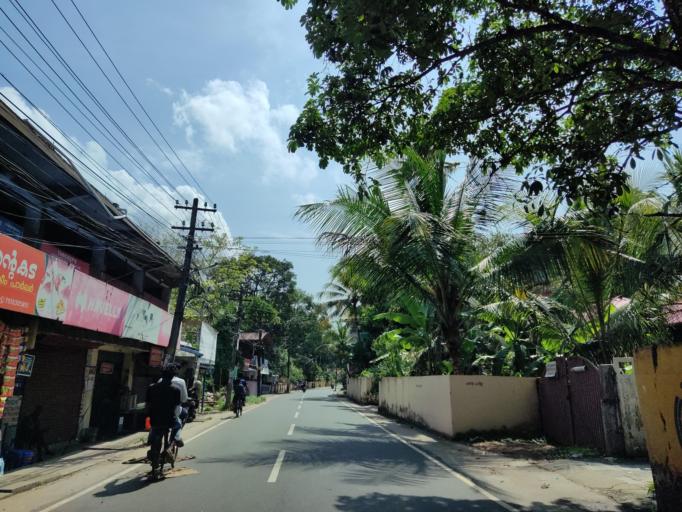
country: IN
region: Kerala
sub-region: Alappuzha
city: Mavelikara
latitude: 9.3196
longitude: 76.5329
